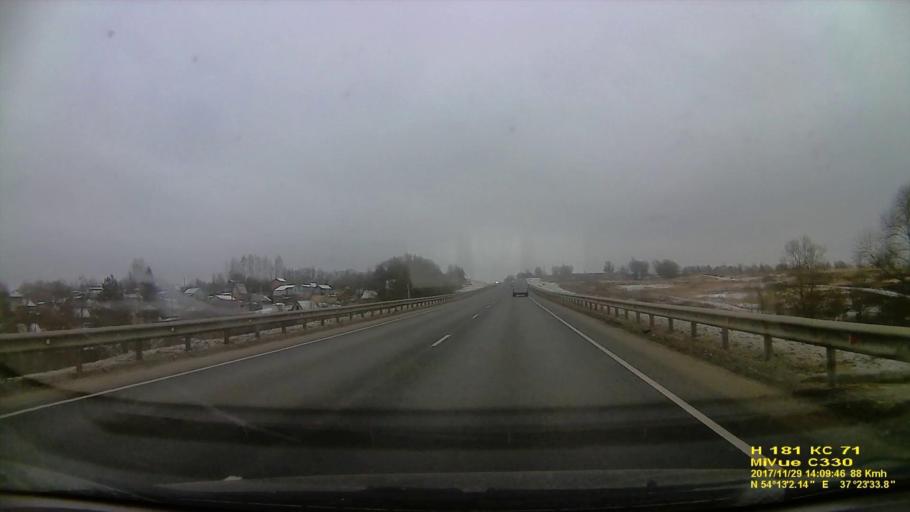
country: RU
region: Tula
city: Leninskiy
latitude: 54.2170
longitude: 37.3930
